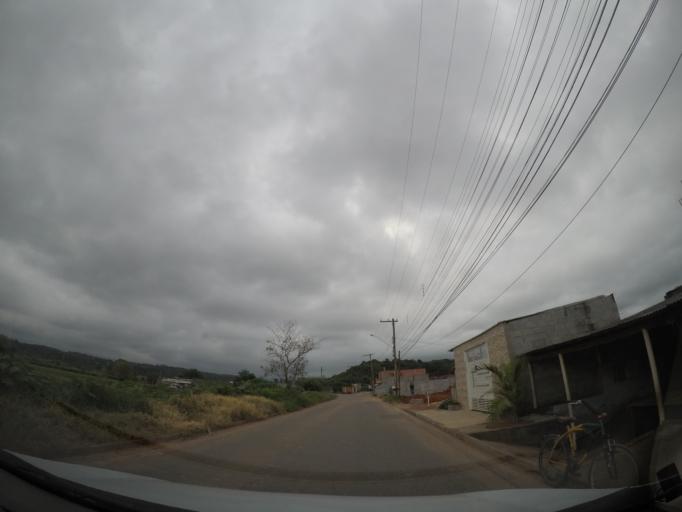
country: BR
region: Sao Paulo
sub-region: Aruja
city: Aruja
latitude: -23.4055
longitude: -46.3607
